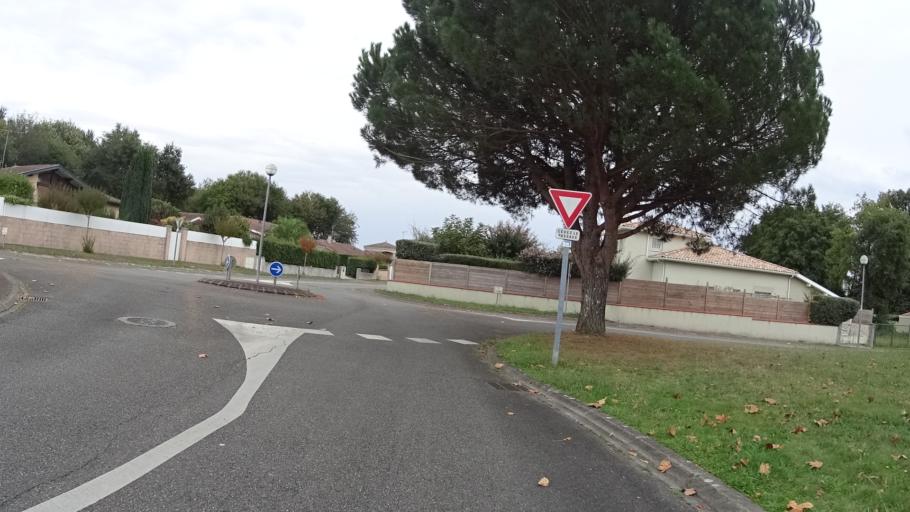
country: FR
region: Aquitaine
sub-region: Departement des Landes
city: Saint-Paul-les-Dax
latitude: 43.7298
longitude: -1.0826
